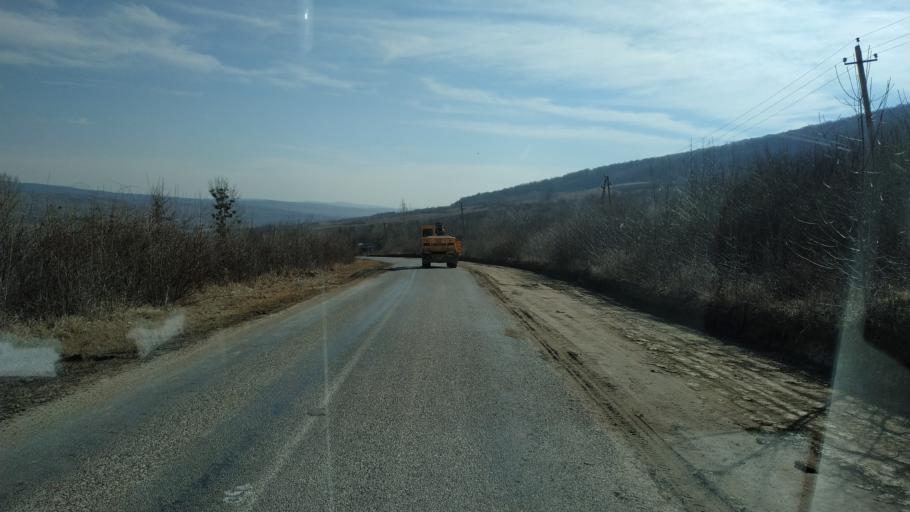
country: MD
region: Nisporeni
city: Nisporeni
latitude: 47.1863
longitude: 28.0719
